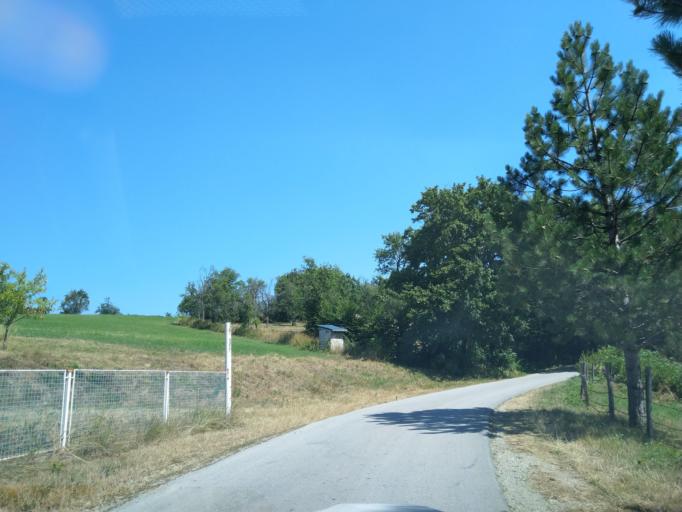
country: RS
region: Central Serbia
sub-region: Zlatiborski Okrug
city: Uzice
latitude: 43.8062
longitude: 19.8329
